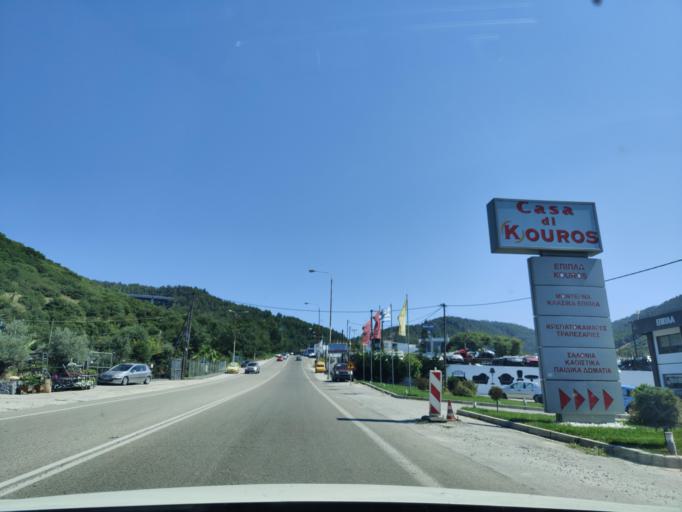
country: GR
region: East Macedonia and Thrace
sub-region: Nomos Kavalas
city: Amygdaleonas
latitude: 40.9547
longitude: 24.3662
